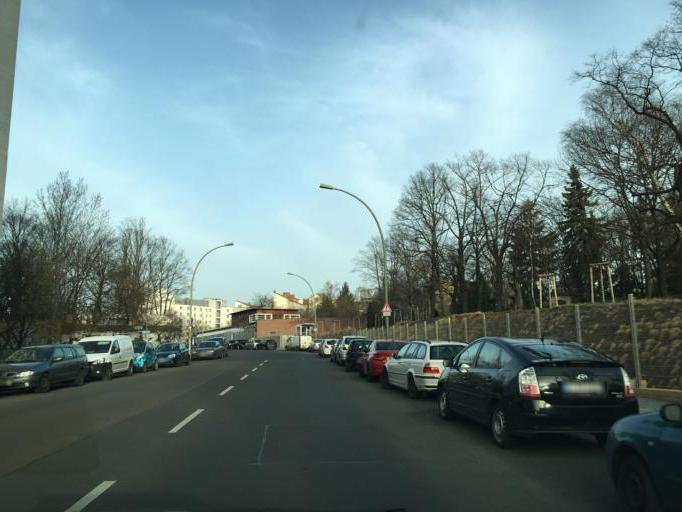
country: DE
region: Berlin
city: Prenzlauer Berg Bezirk
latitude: 52.5286
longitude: 13.4224
